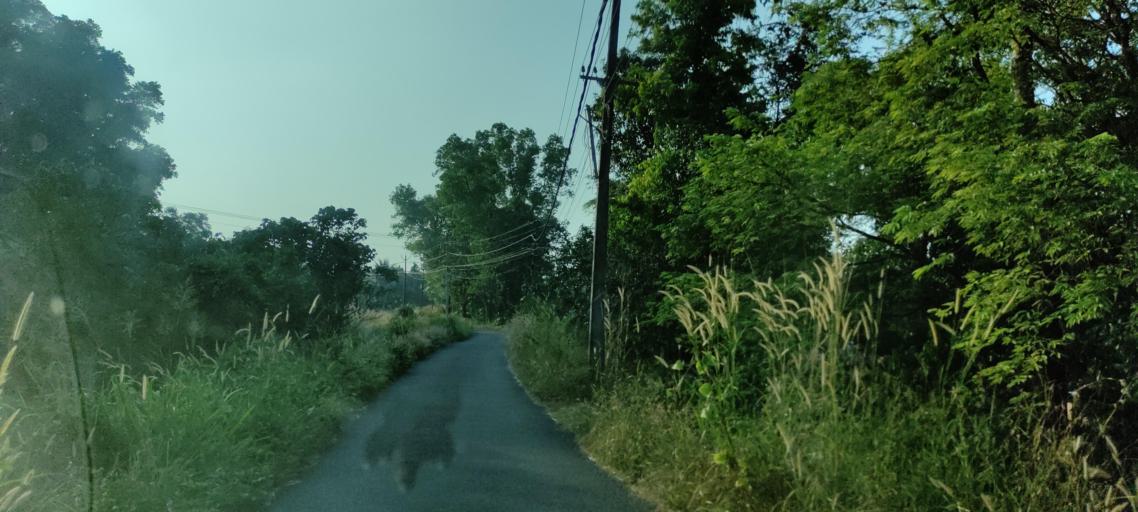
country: IN
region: Kerala
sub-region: Pattanamtitta
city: Adur
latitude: 9.1441
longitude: 76.7366
